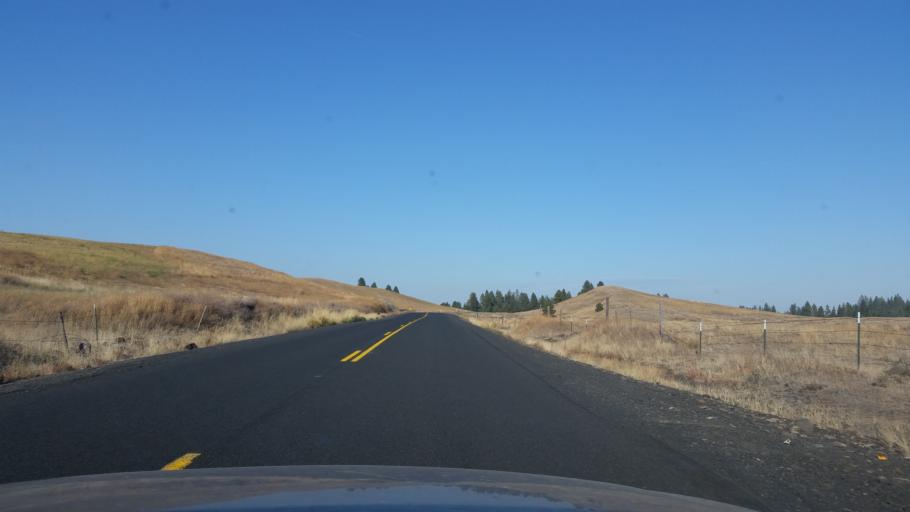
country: US
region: Washington
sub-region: Spokane County
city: Cheney
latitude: 47.3556
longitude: -117.7074
